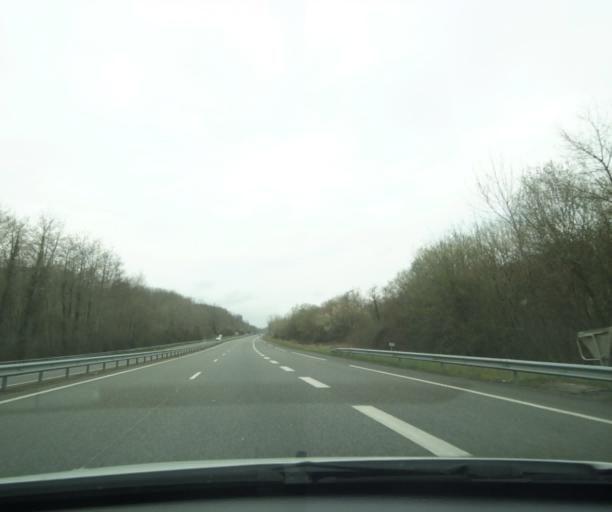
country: FR
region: Aquitaine
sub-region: Departement des Pyrenees-Atlantiques
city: Urt
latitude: 43.4700
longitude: -1.2842
